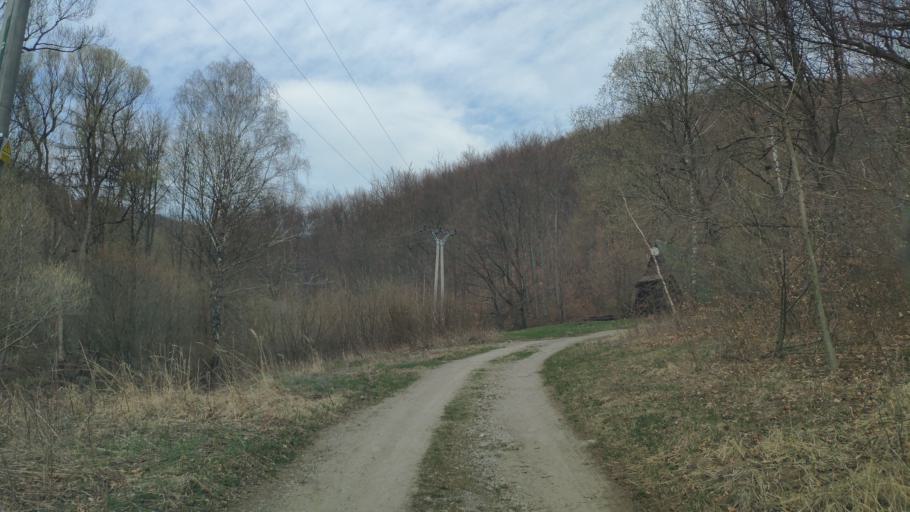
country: SK
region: Kosicky
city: Moldava nad Bodvou
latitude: 48.7489
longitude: 21.0281
